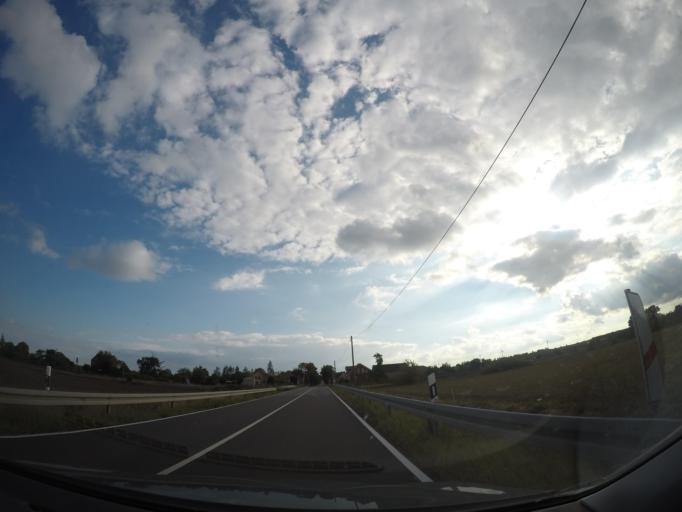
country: DE
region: Saxony-Anhalt
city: Mieste
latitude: 52.4103
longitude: 11.1215
